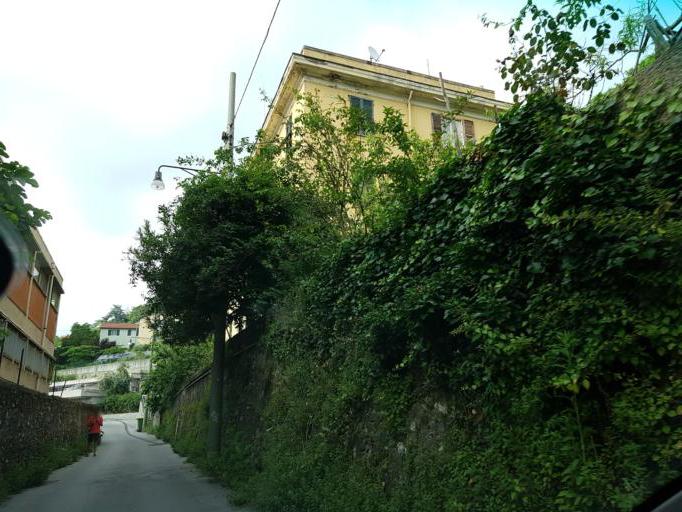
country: IT
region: Liguria
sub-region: Provincia di Genova
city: Genoa
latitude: 44.4455
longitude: 8.8961
